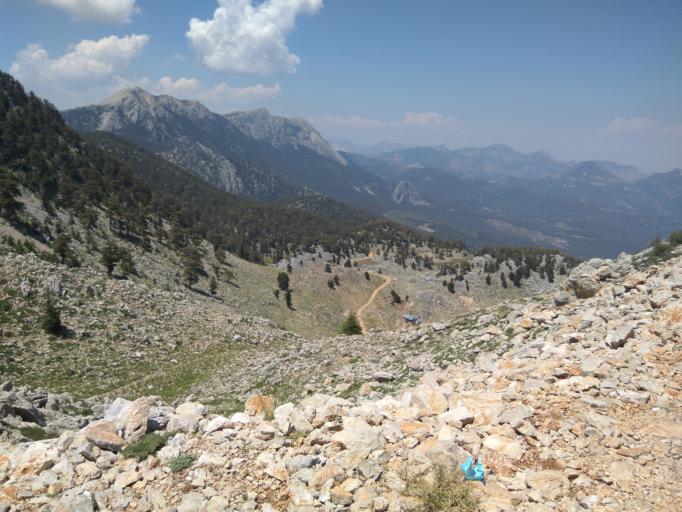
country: TR
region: Antalya
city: Altinyaka
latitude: 36.5431
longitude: 30.4077
